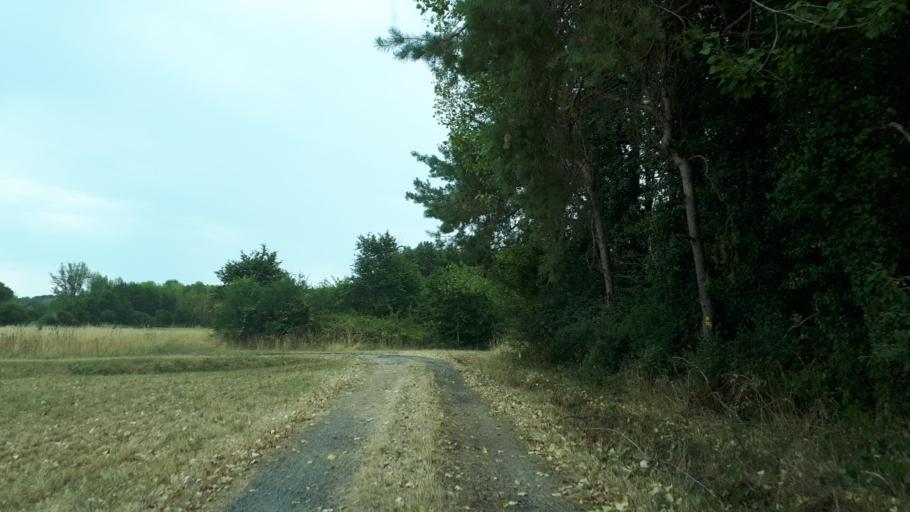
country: FR
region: Centre
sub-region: Departement du Loir-et-Cher
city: Saint-Romain-sur-Cher
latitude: 47.3513
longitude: 1.3966
